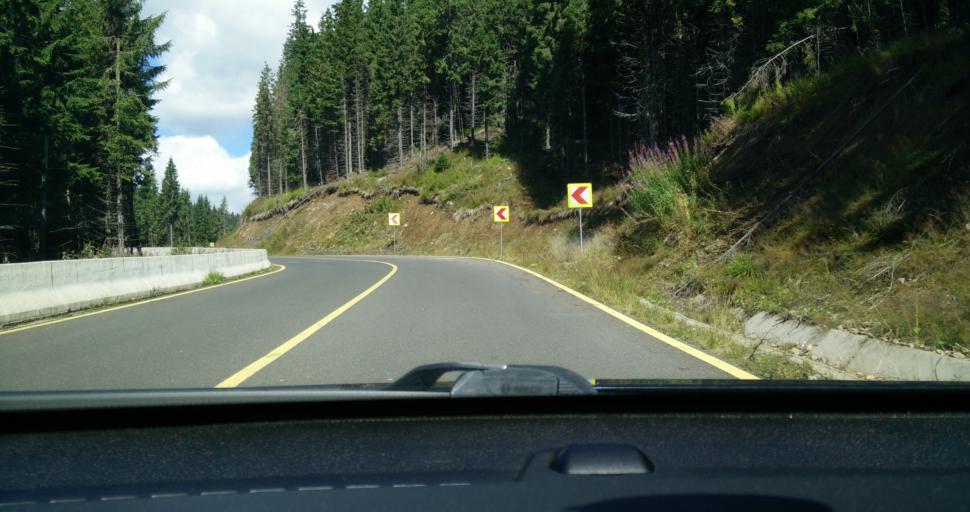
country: RO
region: Hunedoara
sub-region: Oras Petrila
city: Petrila
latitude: 45.4545
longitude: 23.6155
